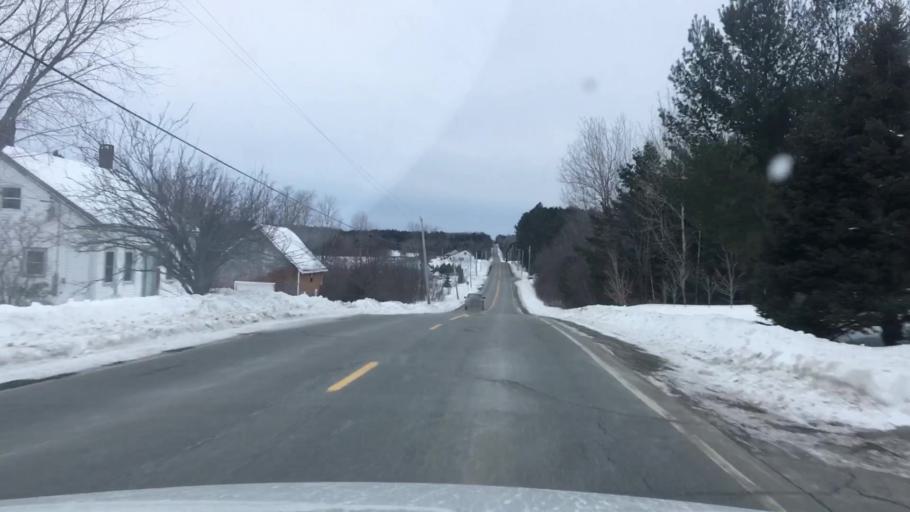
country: US
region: Maine
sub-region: Penobscot County
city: Garland
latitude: 44.9657
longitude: -69.1742
